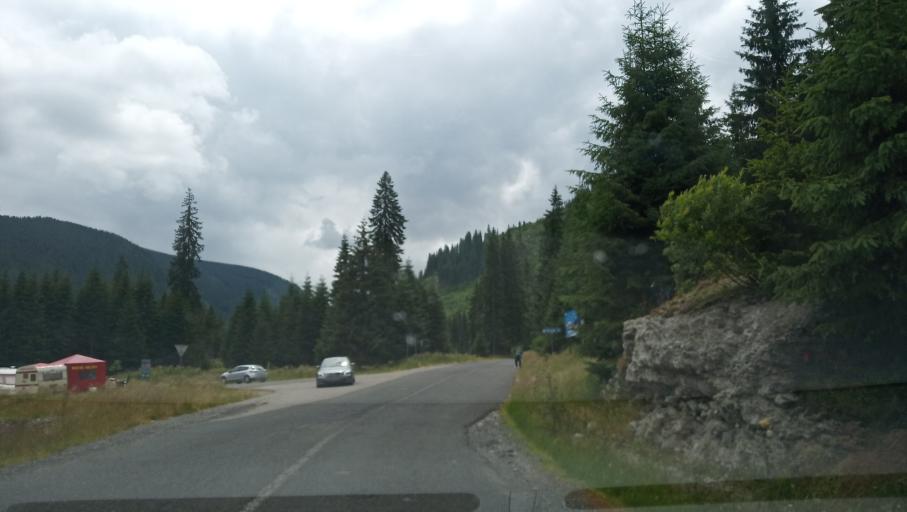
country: RO
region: Hunedoara
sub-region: Oras Petrila
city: Petrila
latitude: 45.4268
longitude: 23.6200
